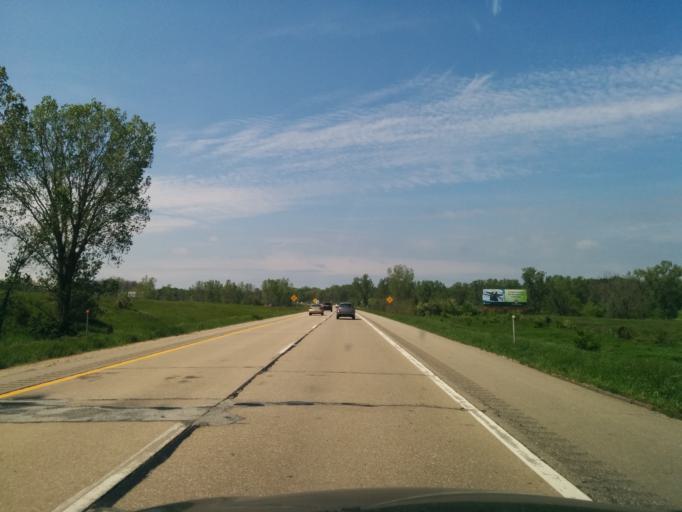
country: US
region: Michigan
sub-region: Ottawa County
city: Holland
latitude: 42.7331
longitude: -86.1451
